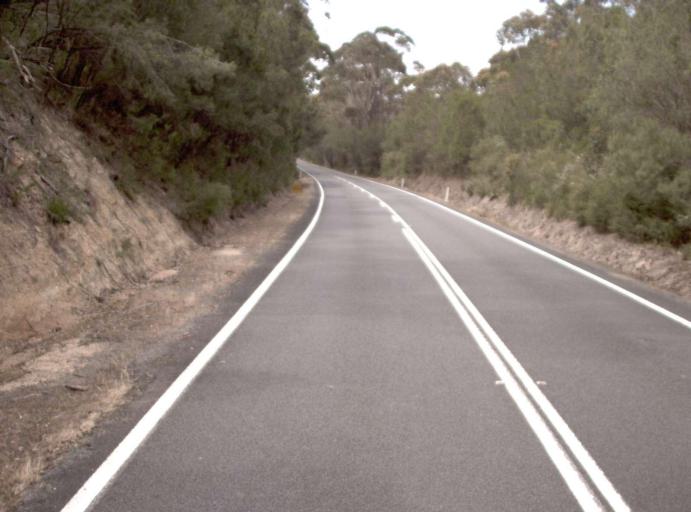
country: AU
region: New South Wales
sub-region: Bega Valley
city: Eden
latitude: -37.4974
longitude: 149.5461
